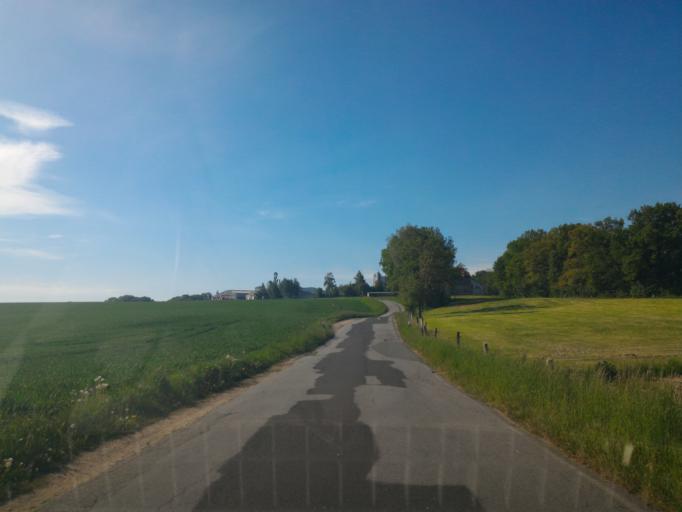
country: DE
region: Saxony
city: Grossschweidnitz
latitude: 51.0600
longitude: 14.6366
